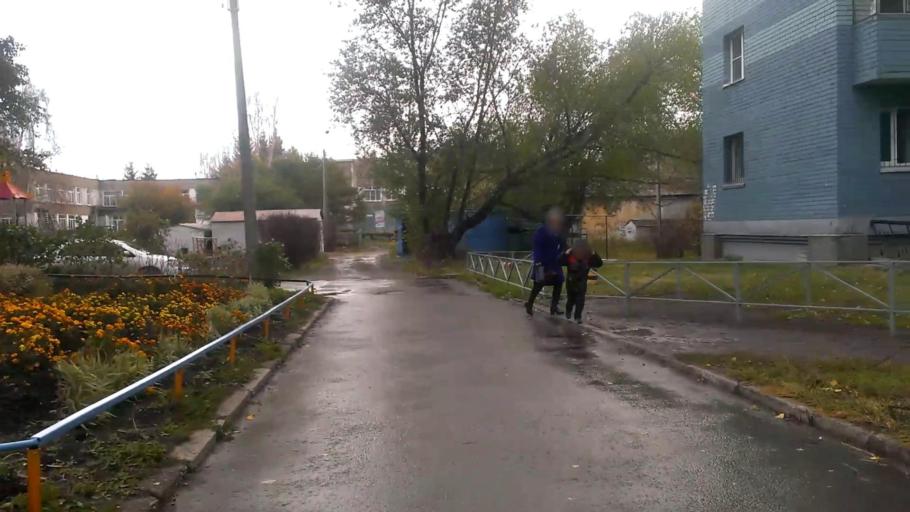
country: RU
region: Altai Krai
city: Novosilikatnyy
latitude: 53.3509
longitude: 83.6736
